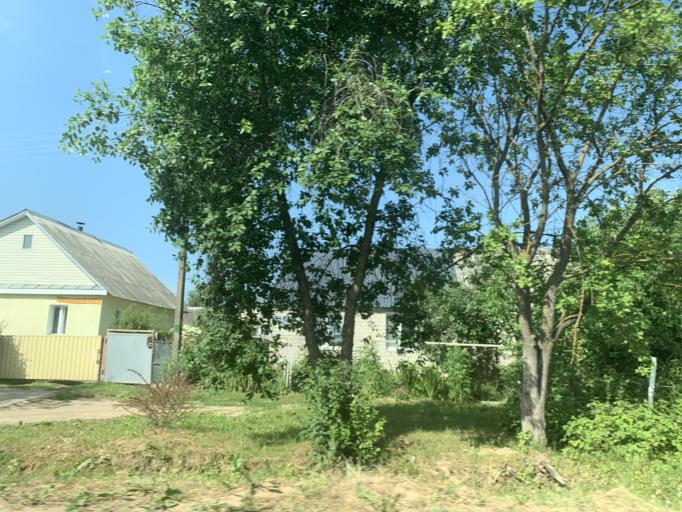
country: BY
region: Minsk
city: Dzyarzhynsk
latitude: 53.6993
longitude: 27.1010
